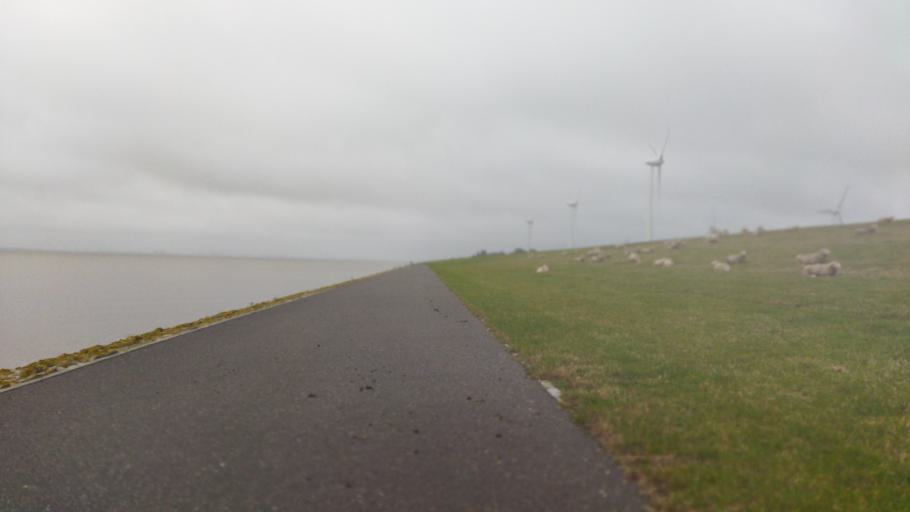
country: DE
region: Lower Saxony
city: Emden
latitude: 53.3349
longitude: 7.0966
